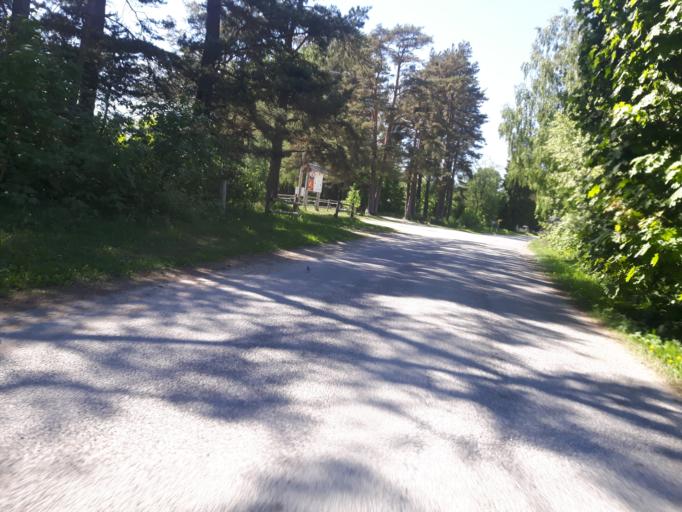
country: EE
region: Laeaene-Virumaa
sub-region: Haljala vald
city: Haljala
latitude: 59.5494
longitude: 26.3794
